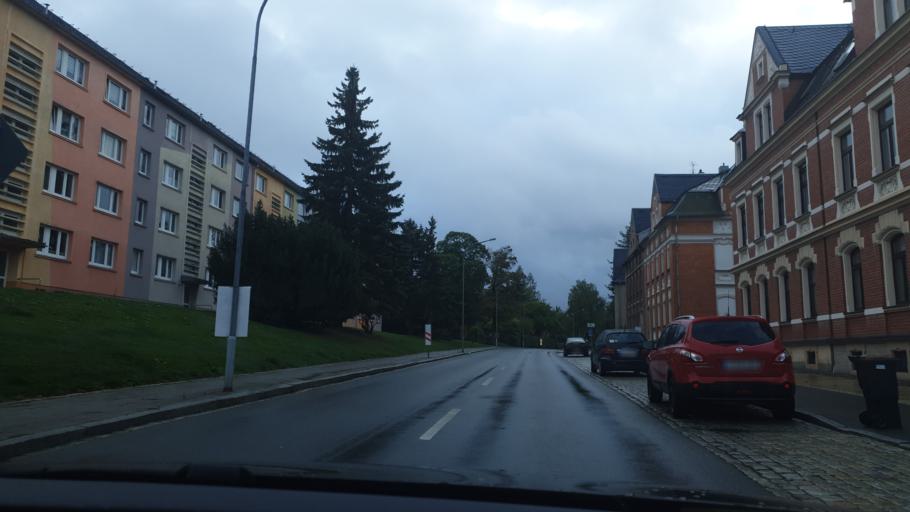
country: DE
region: Saxony
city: Falkenstein
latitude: 50.4711
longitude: 12.3646
